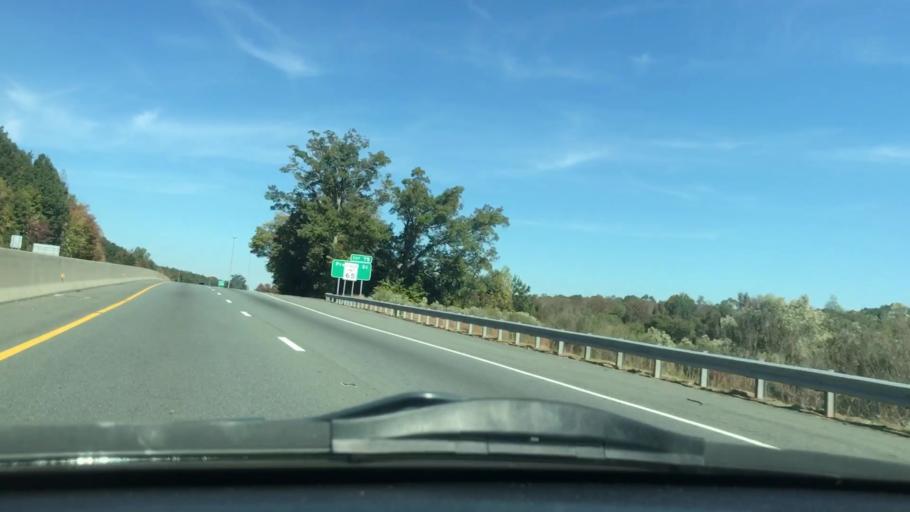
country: US
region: North Carolina
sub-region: Randolph County
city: Asheboro
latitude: 35.7146
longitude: -79.8268
